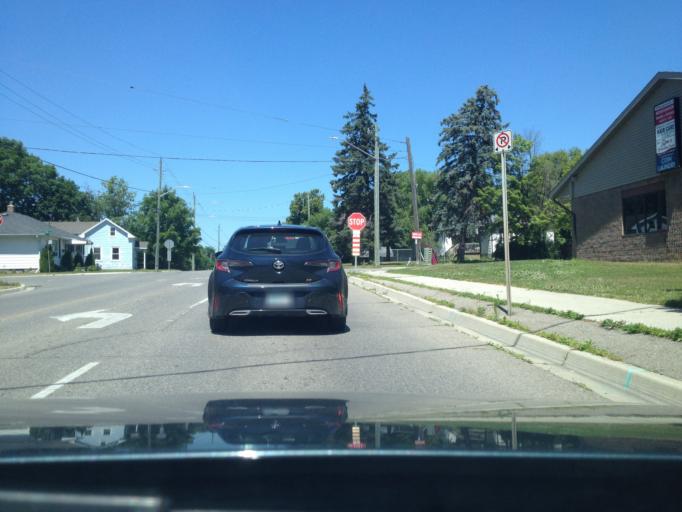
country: CA
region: Ontario
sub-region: Halton
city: Milton
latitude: 43.6601
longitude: -79.9166
